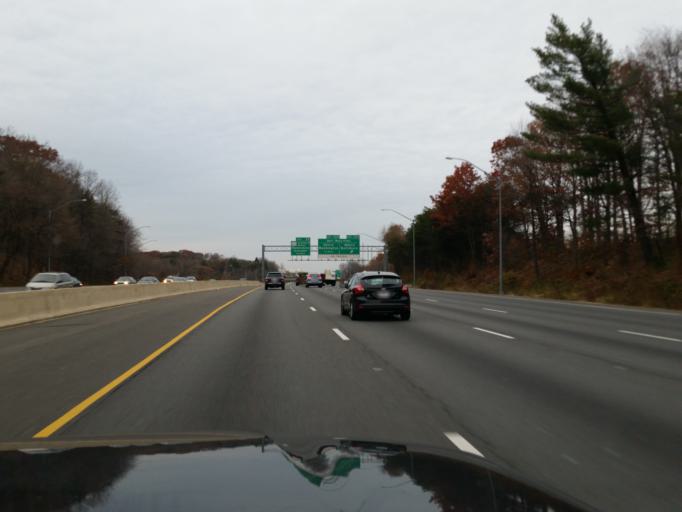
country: US
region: Maryland
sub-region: Prince George's County
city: Greenbelt
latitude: 38.9878
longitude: -76.8828
